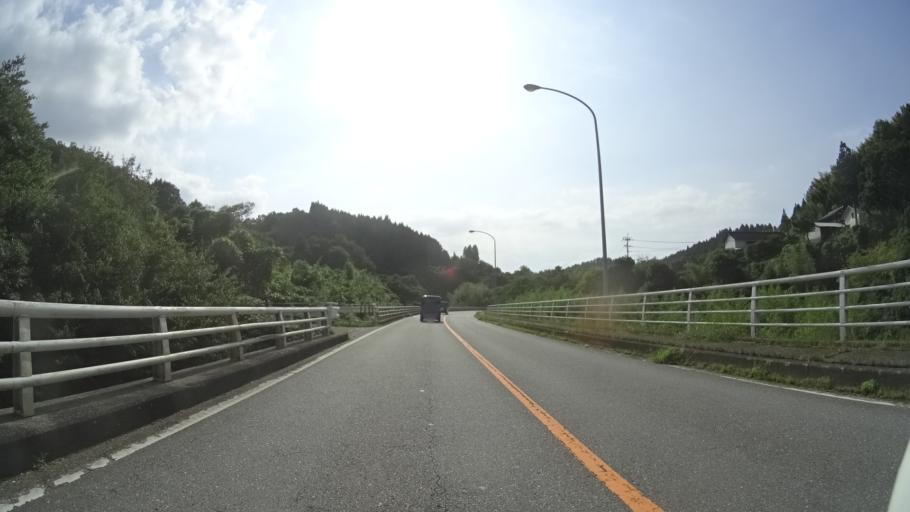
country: JP
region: Kumamoto
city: Aso
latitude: 32.6881
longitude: 131.0730
